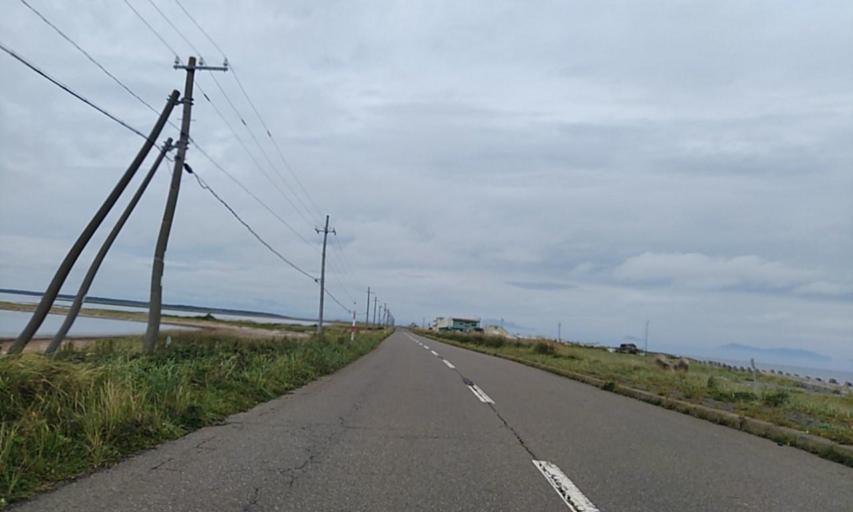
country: JP
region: Hokkaido
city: Shibetsu
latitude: 43.5918
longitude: 145.3333
